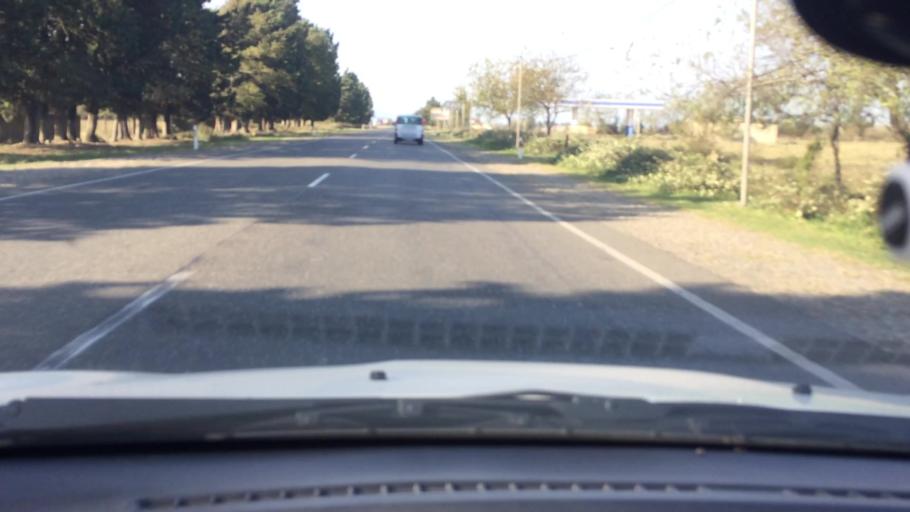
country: GE
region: Imereti
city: Kutaisi
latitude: 42.2299
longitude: 42.6013
